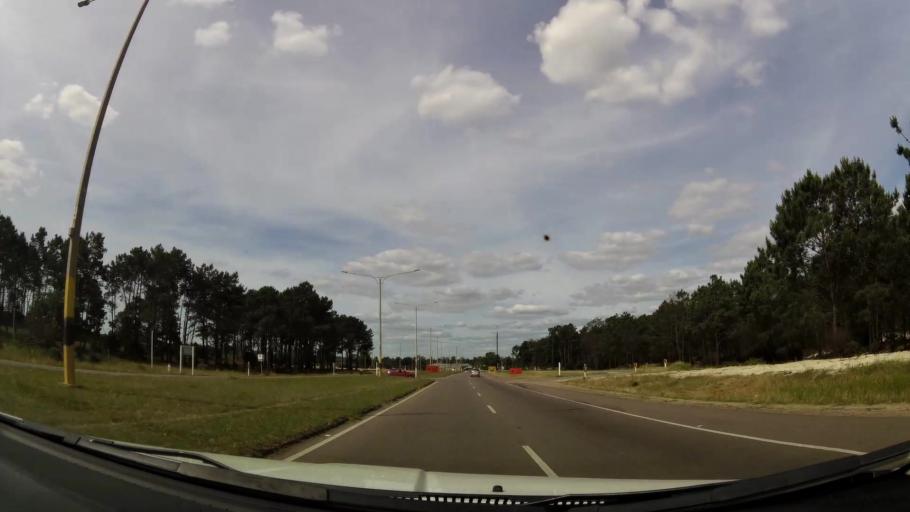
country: UY
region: Canelones
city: Empalme Olmos
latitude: -34.7904
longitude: -55.8966
